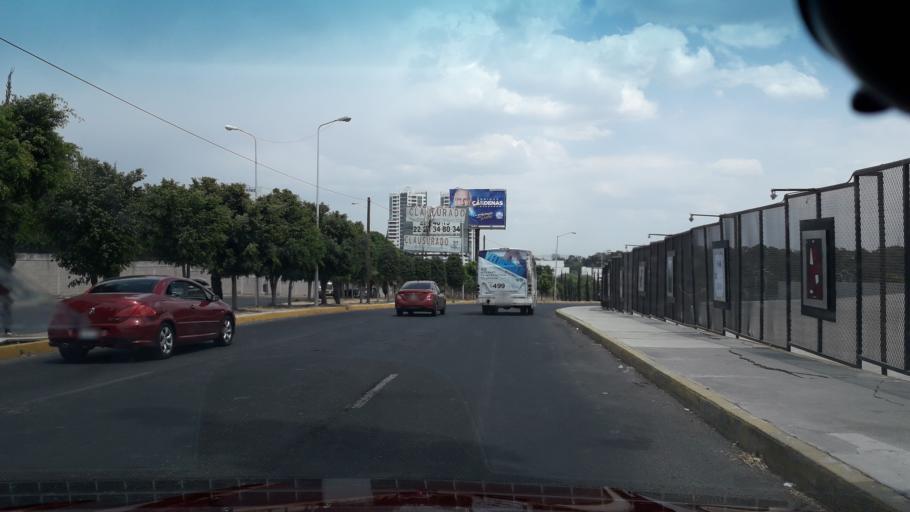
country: MX
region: Puebla
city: Puebla
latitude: 19.0212
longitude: -98.2395
